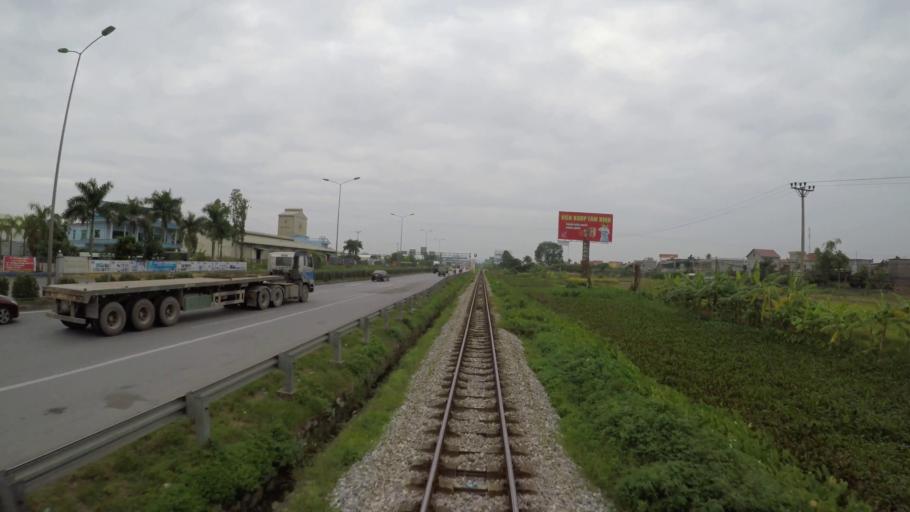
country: VN
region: Hai Duong
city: Nam Sach
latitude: 20.9669
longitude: 106.3780
